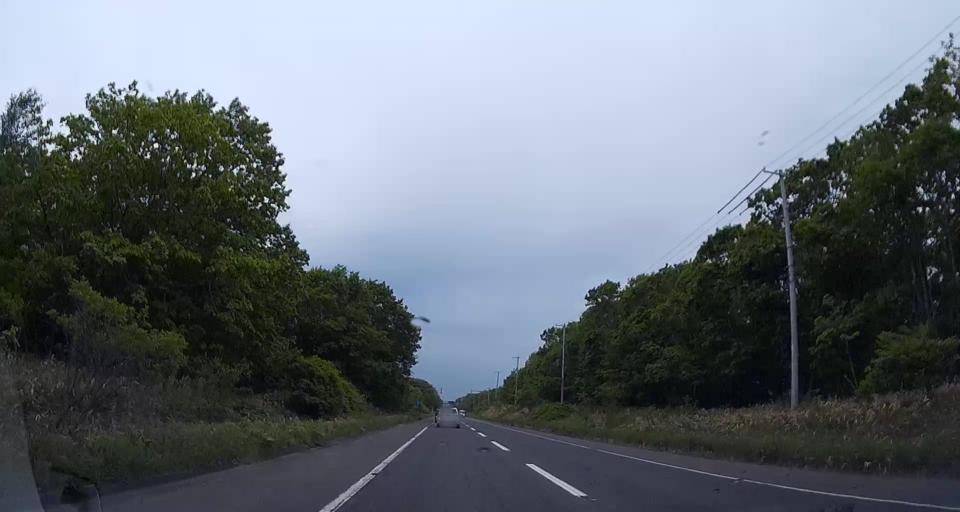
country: JP
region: Hokkaido
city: Tomakomai
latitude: 42.6953
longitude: 141.7363
